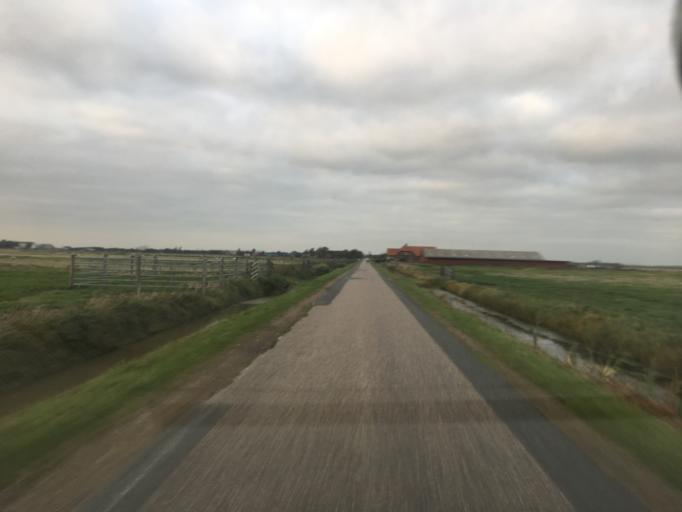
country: DE
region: Schleswig-Holstein
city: Klanxbull
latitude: 54.9446
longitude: 8.6876
